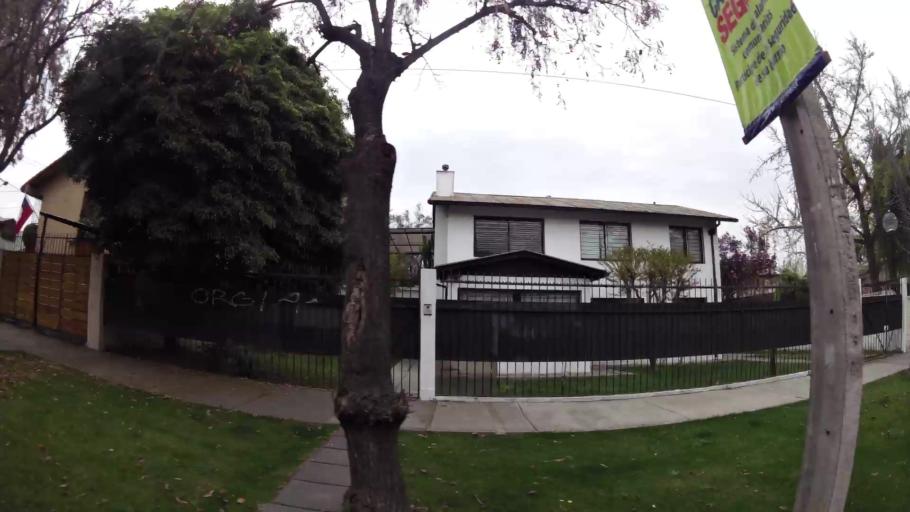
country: CL
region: Santiago Metropolitan
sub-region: Provincia de Santiago
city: Villa Presidente Frei, Nunoa, Santiago, Chile
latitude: -33.4603
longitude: -70.5903
